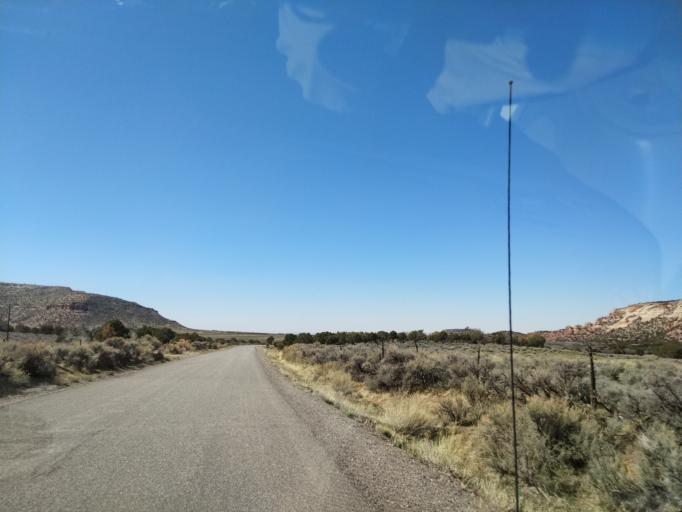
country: US
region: Colorado
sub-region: Mesa County
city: Loma
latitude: 38.9563
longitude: -109.0214
